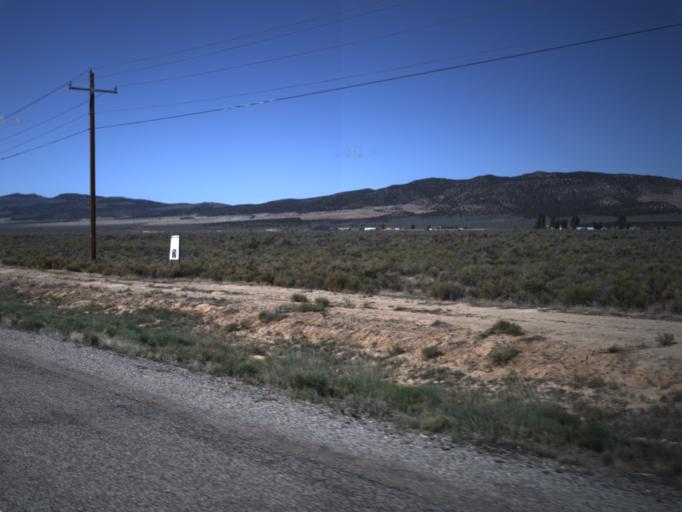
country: US
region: Utah
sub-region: Iron County
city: Cedar City
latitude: 37.6823
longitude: -113.1675
